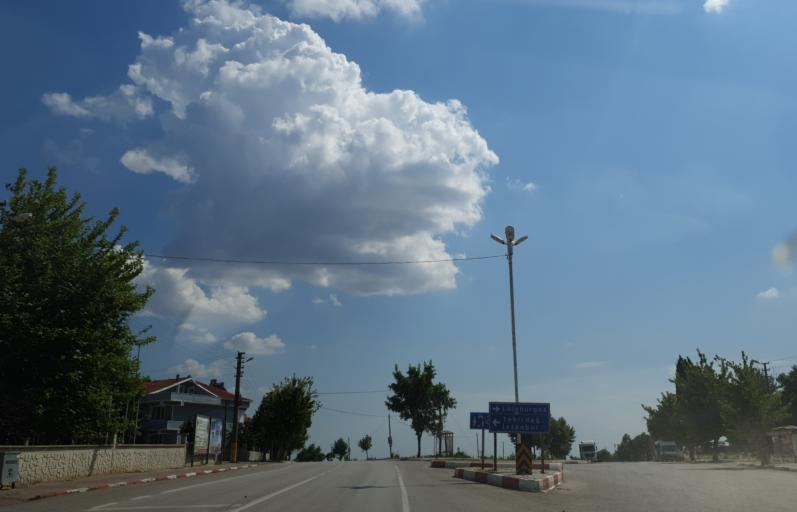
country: TR
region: Kirklareli
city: Buyukkaristiran
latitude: 41.4360
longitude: 27.5840
